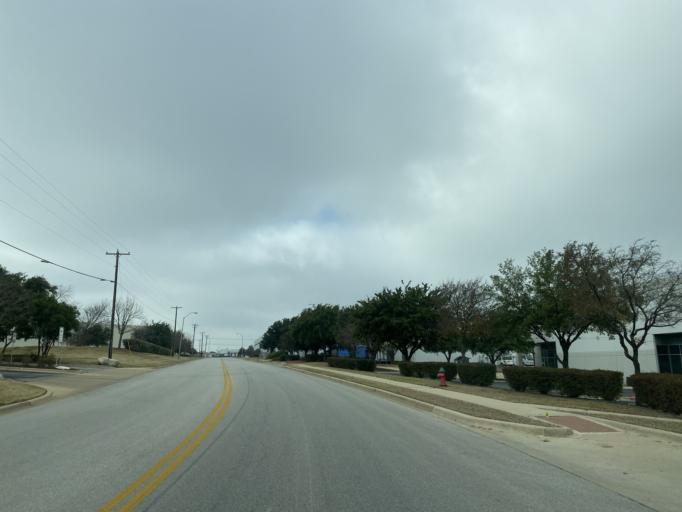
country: US
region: Texas
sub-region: Williamson County
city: Round Rock
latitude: 30.5372
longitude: -97.6846
